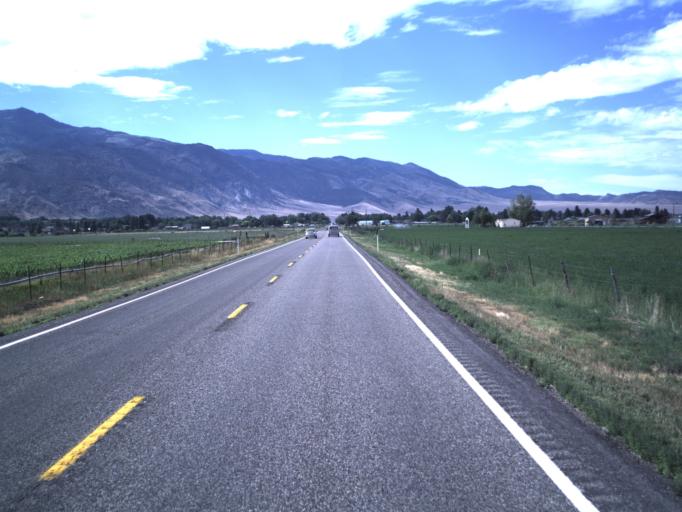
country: US
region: Utah
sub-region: Sevier County
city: Monroe
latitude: 38.6529
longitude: -112.1215
